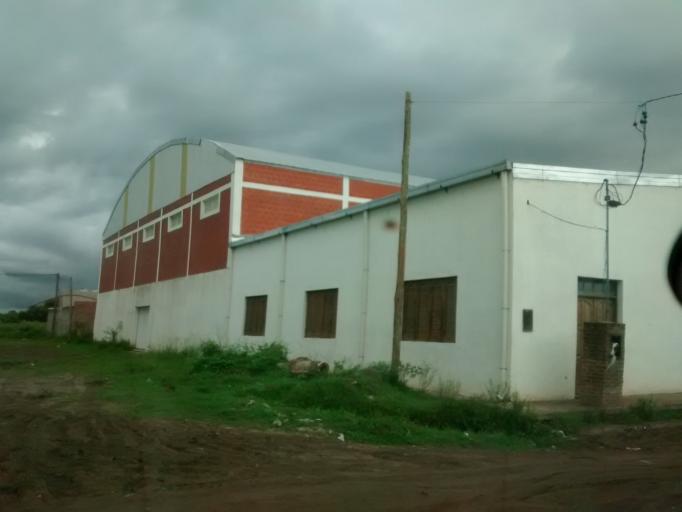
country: AR
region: Chaco
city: Puerto Tirol
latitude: -27.3800
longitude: -59.0932
